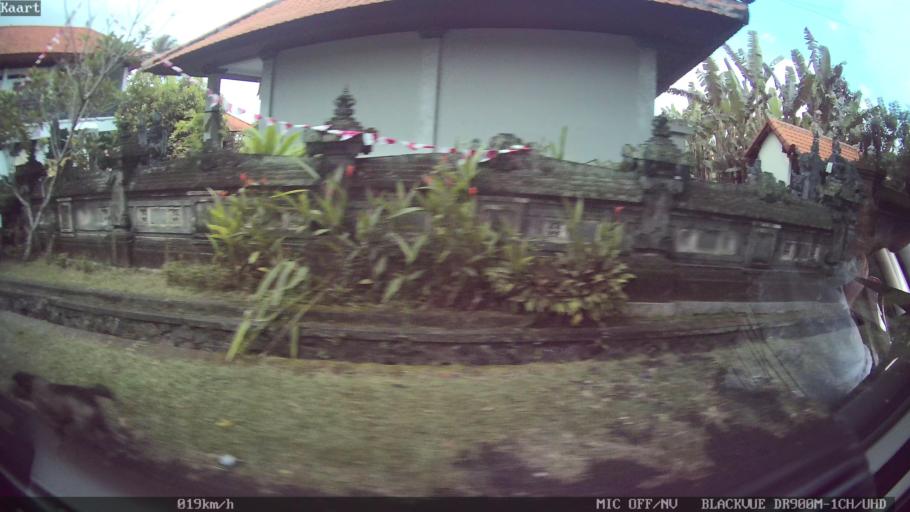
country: ID
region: Bali
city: Banjar Bucu
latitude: -8.5923
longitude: 115.2096
